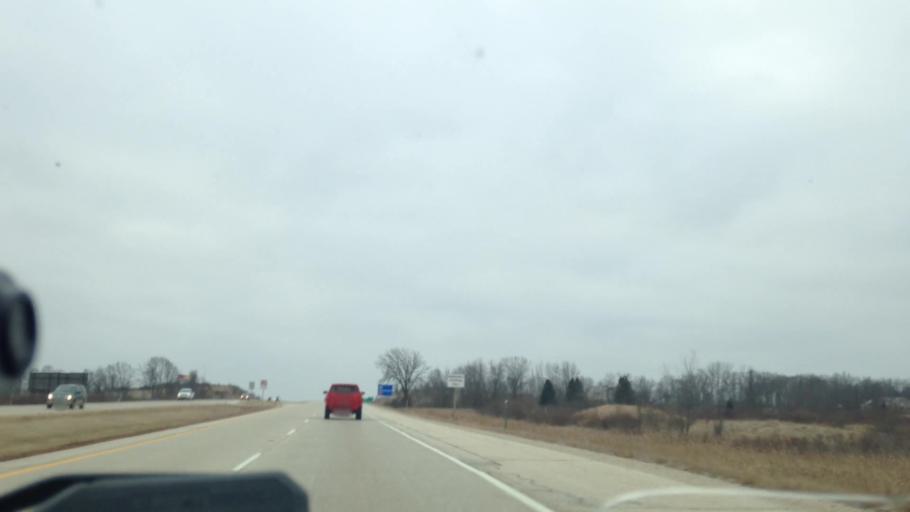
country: US
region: Wisconsin
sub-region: Washington County
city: Jackson
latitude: 43.2939
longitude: -88.1873
